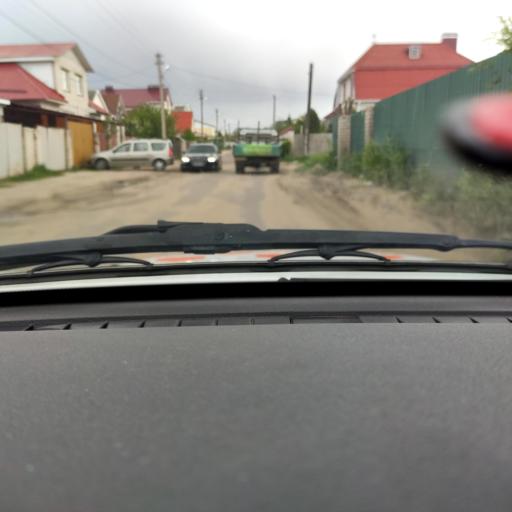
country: RU
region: Voronezj
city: Podgornoye
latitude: 51.7419
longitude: 39.1640
